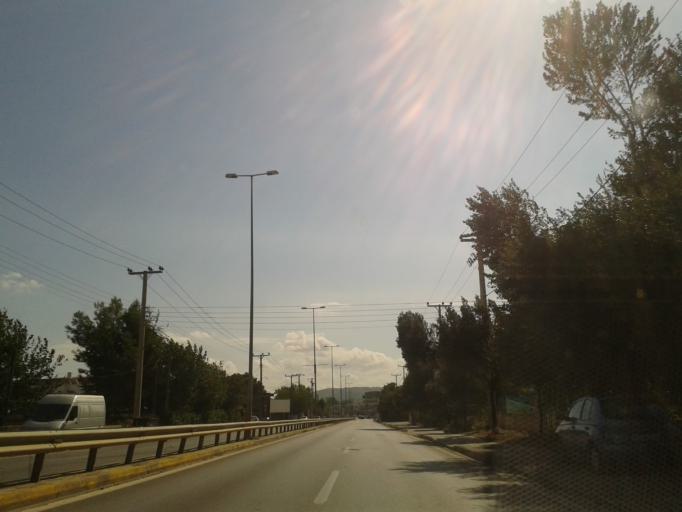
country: GR
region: Attica
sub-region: Nomarchia Anatolikis Attikis
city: Aghios Panteleimon
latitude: 38.1074
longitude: 23.9693
